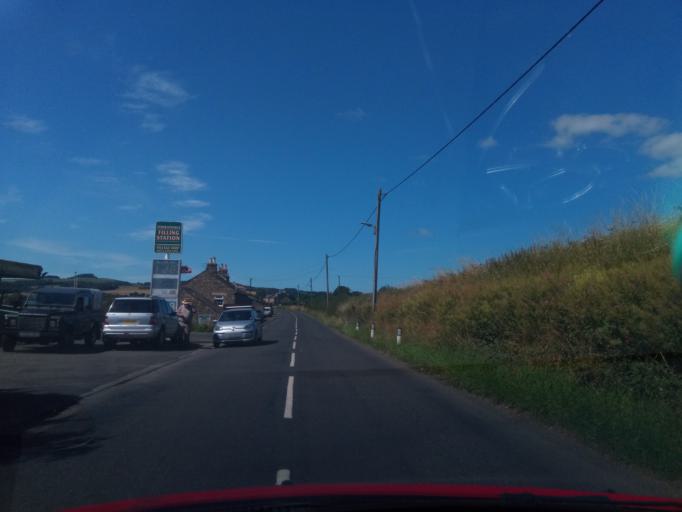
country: GB
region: England
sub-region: Northumberland
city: Wall
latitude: 55.0055
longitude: -2.1776
